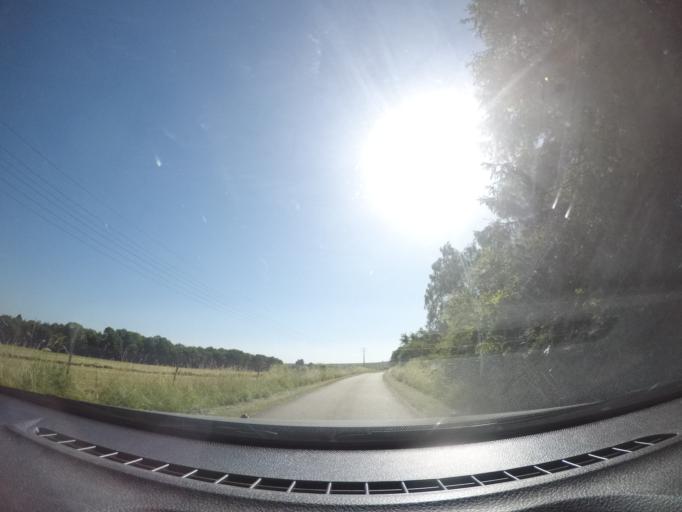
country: BE
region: Wallonia
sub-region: Province de Namur
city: Philippeville
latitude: 50.1861
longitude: 4.5990
